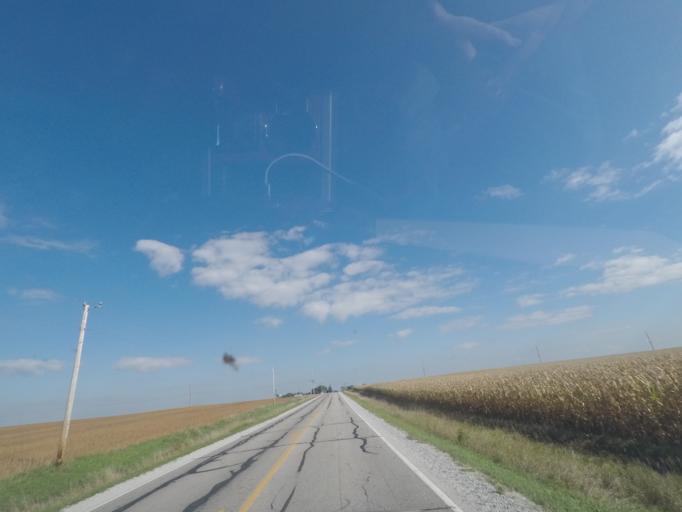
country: US
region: Iowa
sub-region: Story County
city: Nevada
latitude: 42.0324
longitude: -93.4058
